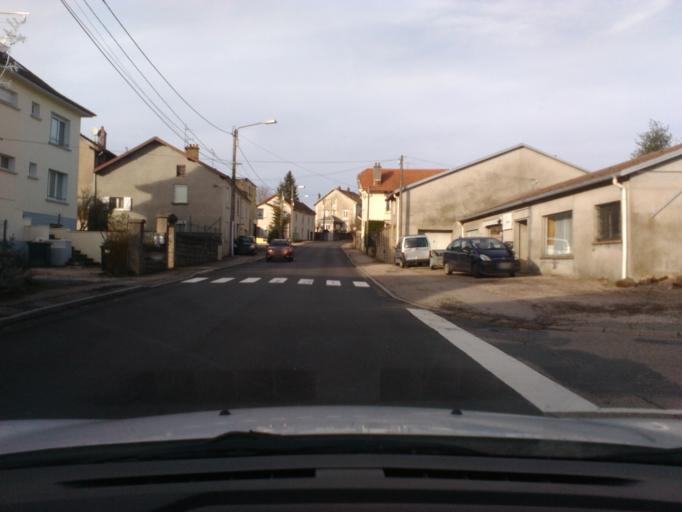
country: FR
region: Lorraine
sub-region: Departement des Vosges
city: Bruyeres
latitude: 48.2050
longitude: 6.7224
